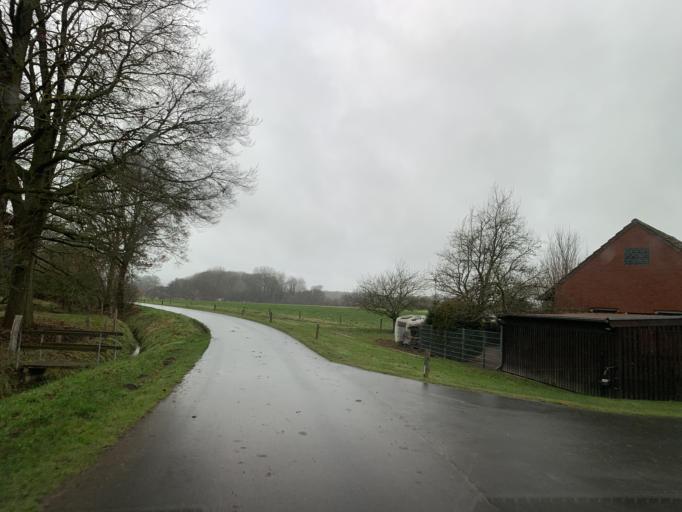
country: DE
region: North Rhine-Westphalia
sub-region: Regierungsbezirk Munster
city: Havixbeck
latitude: 51.9450
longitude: 7.4939
